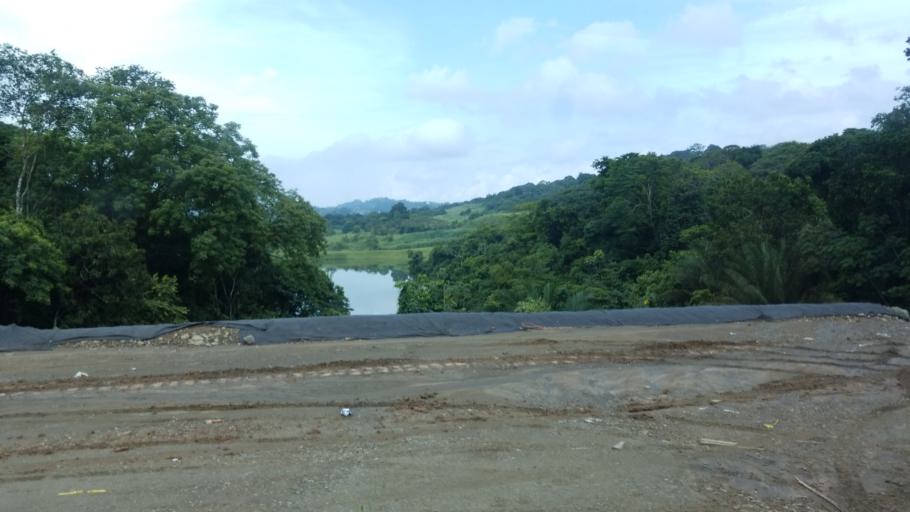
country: PA
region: Panama
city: Las Cumbres
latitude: 9.1028
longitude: -79.5233
